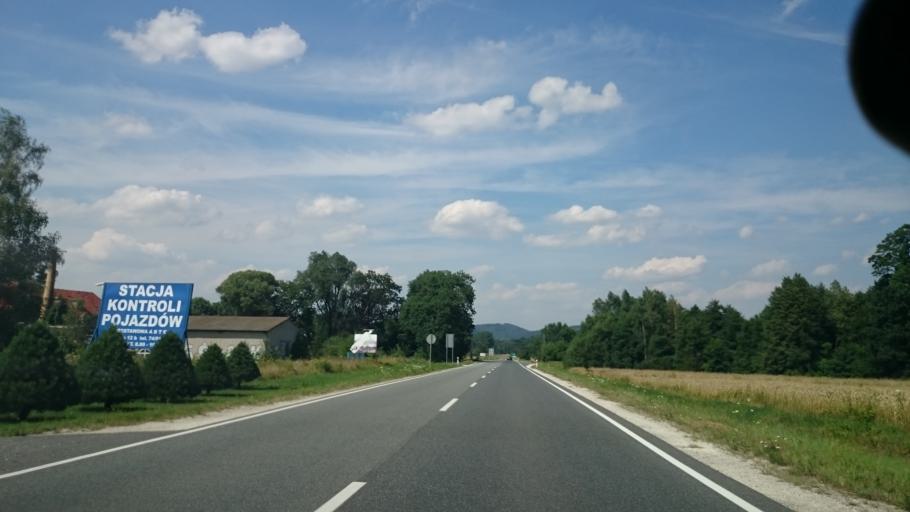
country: PL
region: Lower Silesian Voivodeship
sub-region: Powiat klodzki
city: Bystrzyca Klodzka
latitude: 50.3086
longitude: 16.6602
